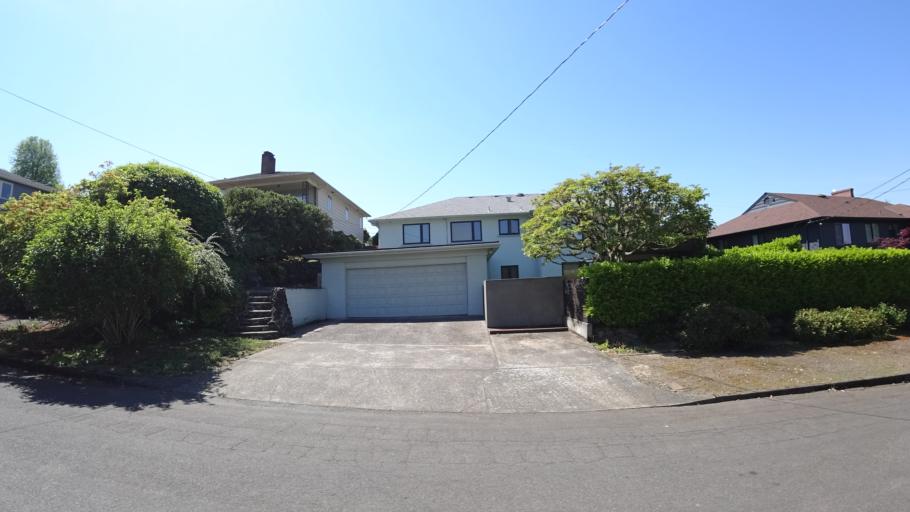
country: US
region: Oregon
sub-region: Clackamas County
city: Milwaukie
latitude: 45.4661
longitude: -122.6805
